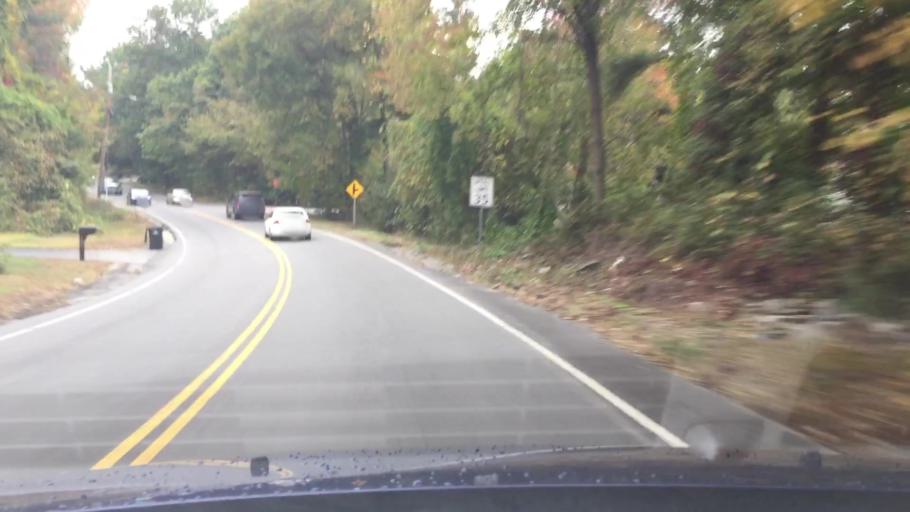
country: US
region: Massachusetts
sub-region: Middlesex County
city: Tyngsboro
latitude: 42.7024
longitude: -71.3905
